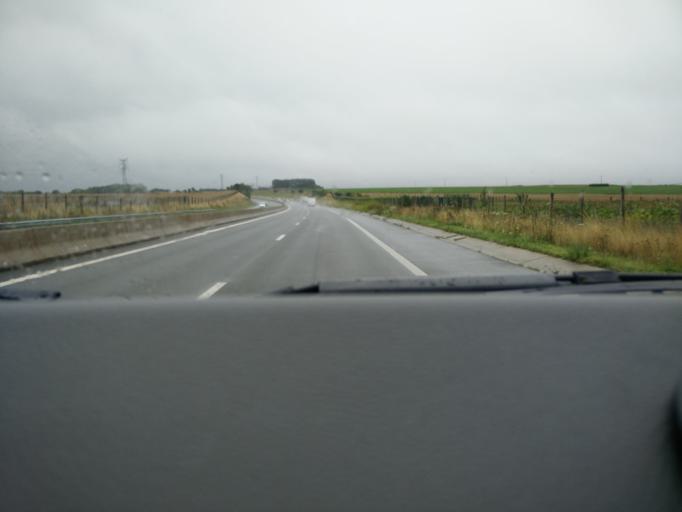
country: FR
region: Nord-Pas-de-Calais
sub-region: Departement du Pas-de-Calais
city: Marconnelle
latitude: 50.3628
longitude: 1.9721
